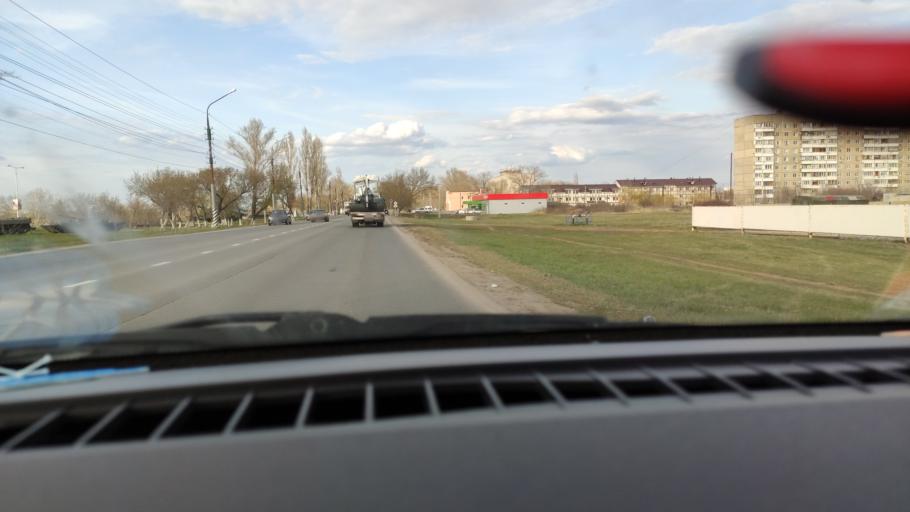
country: RU
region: Saratov
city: Engel's
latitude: 51.4475
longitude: 46.0777
